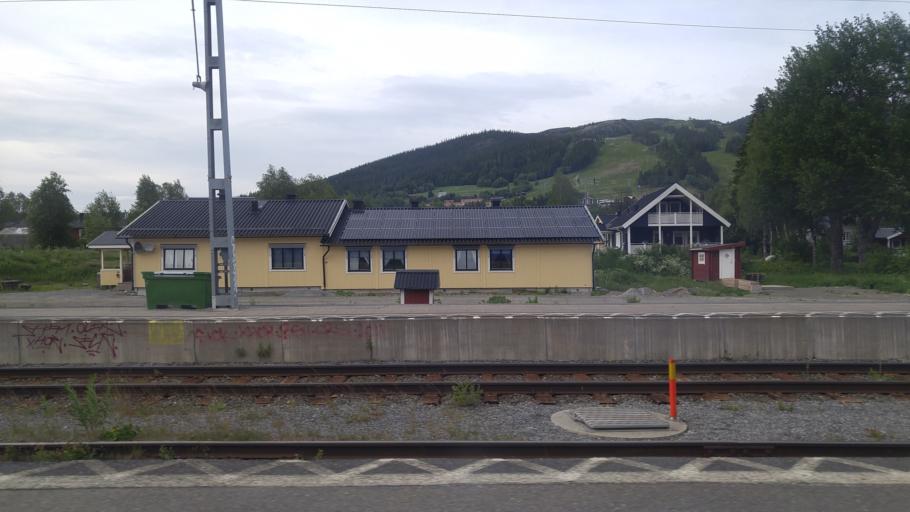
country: SE
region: Jaemtland
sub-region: Are Kommun
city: Are
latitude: 63.3898
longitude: 12.9216
